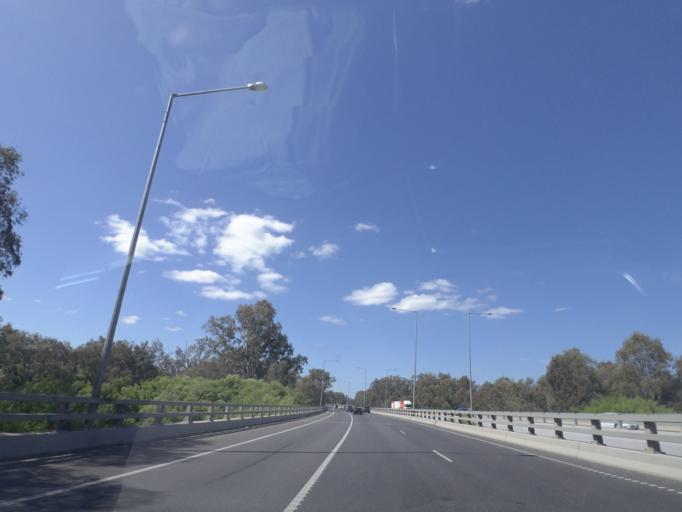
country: AU
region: New South Wales
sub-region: Albury Municipality
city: South Albury
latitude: -36.1067
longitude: 146.9040
